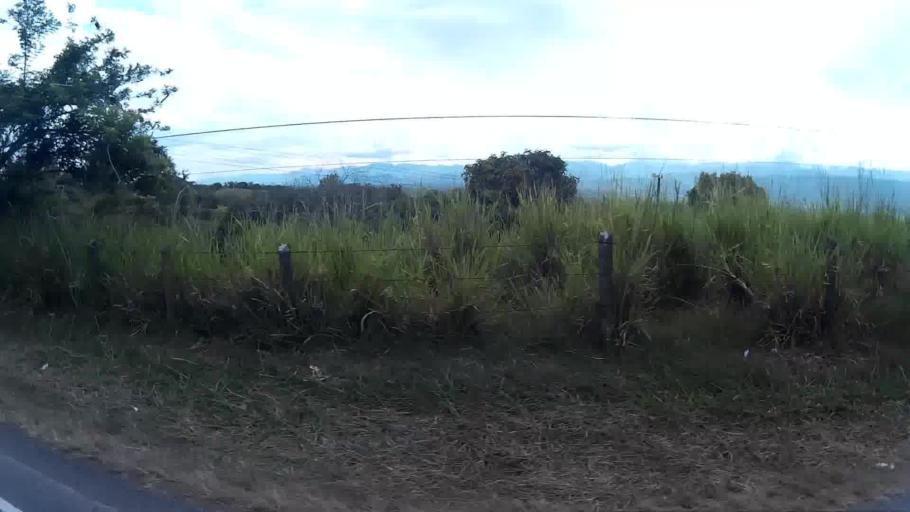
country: CO
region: Risaralda
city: La Virginia
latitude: 4.8556
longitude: -75.8677
